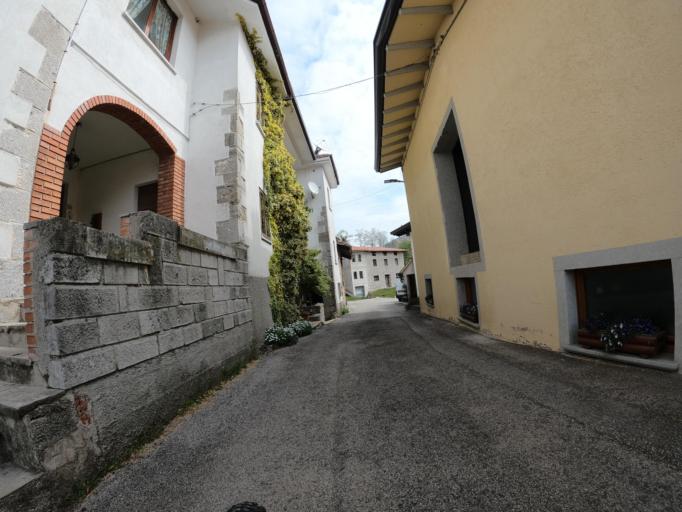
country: IT
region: Friuli Venezia Giulia
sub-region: Provincia di Udine
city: Clodig
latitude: 46.1419
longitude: 13.6034
